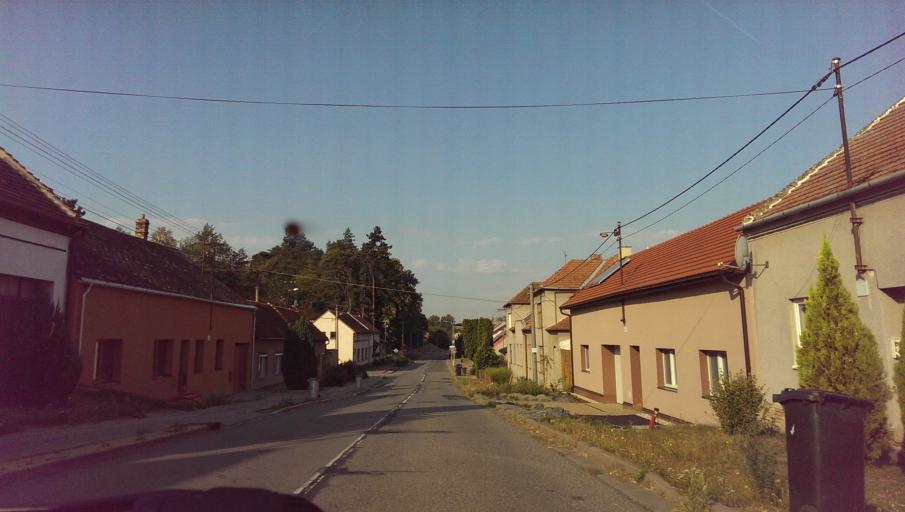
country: CZ
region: South Moravian
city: Nesovice
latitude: 49.1485
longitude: 17.0861
